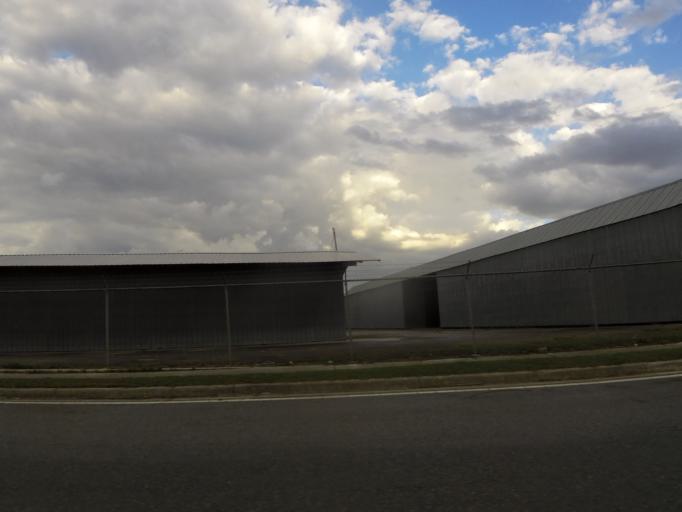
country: US
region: Florida
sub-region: Duval County
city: Jacksonville
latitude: 30.2637
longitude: -81.6207
